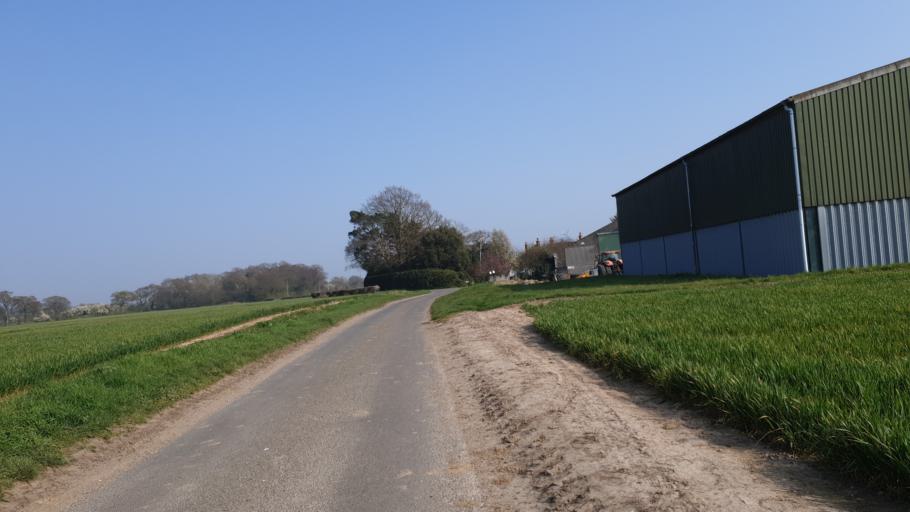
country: GB
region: England
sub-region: Essex
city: Mistley
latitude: 51.8917
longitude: 1.1211
